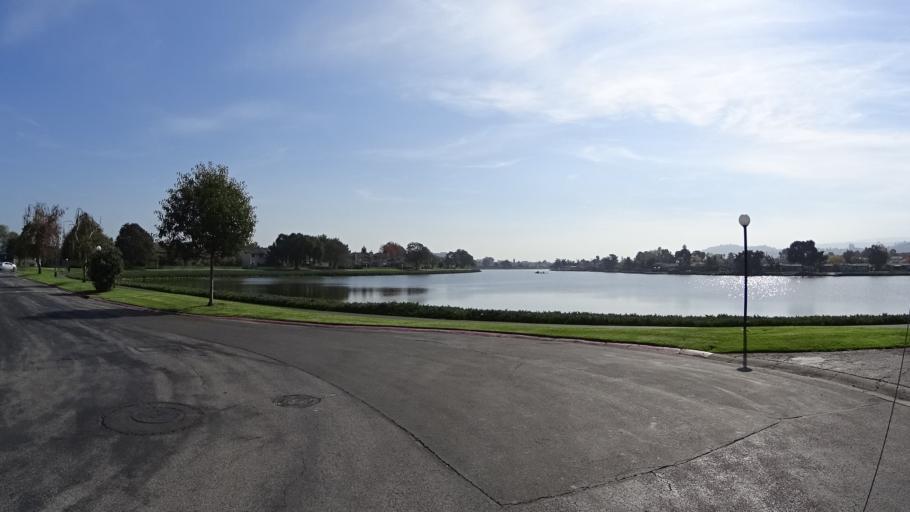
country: US
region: California
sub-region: San Mateo County
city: Foster City
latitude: 37.5488
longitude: -122.2815
